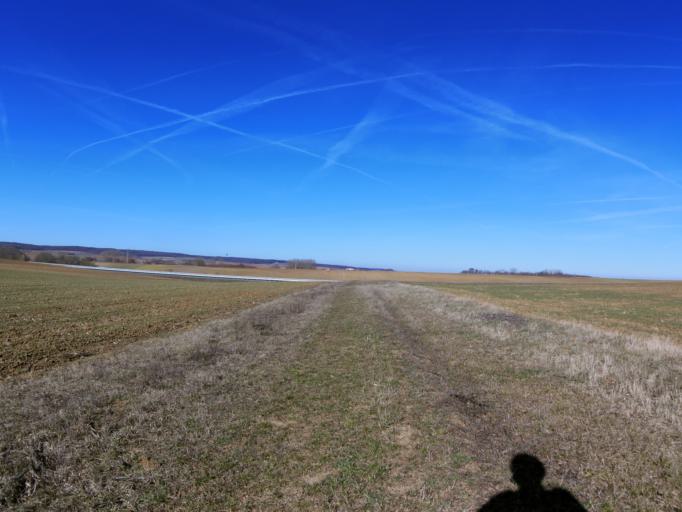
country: DE
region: Bavaria
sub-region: Regierungsbezirk Unterfranken
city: Kurnach
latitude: 49.8568
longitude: 10.0313
